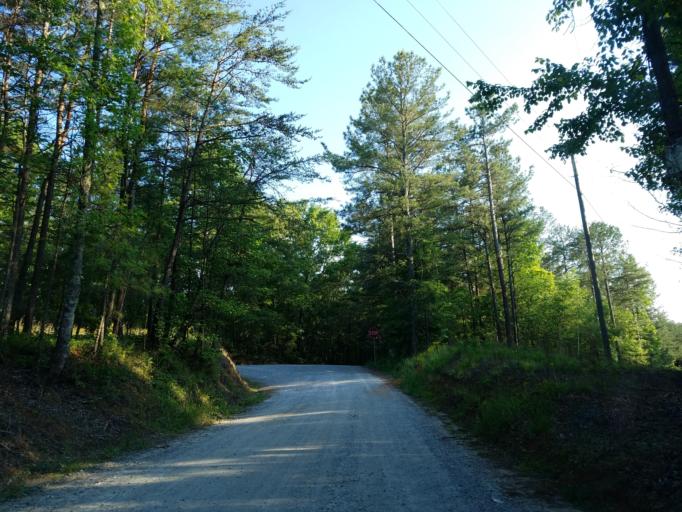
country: US
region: Georgia
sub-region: Cherokee County
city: Ball Ground
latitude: 34.3446
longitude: -84.3250
